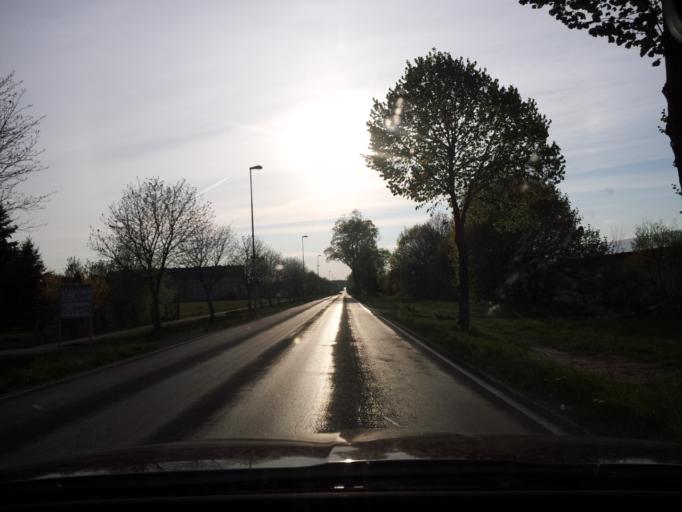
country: DE
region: Brandenburg
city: Drahnsdorf
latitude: 51.8500
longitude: 13.5329
